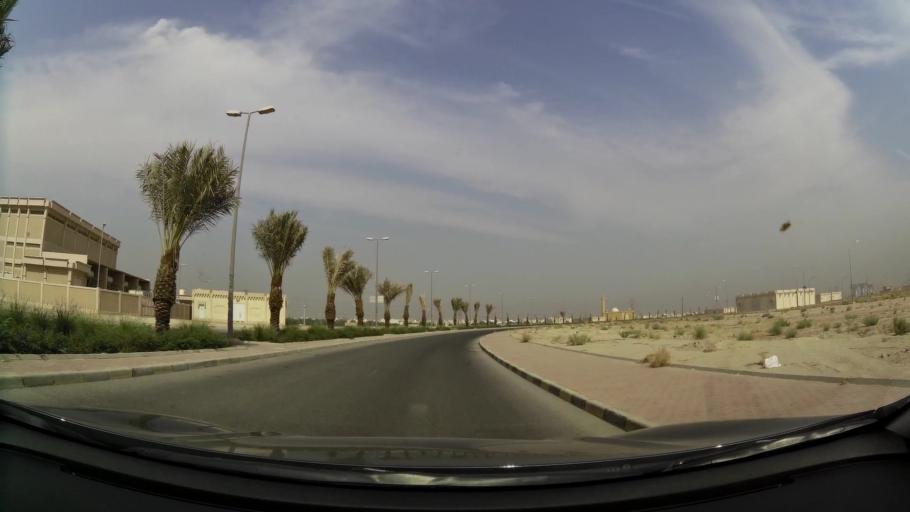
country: KW
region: Al Farwaniyah
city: Janub as Surrah
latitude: 29.2969
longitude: 47.9826
